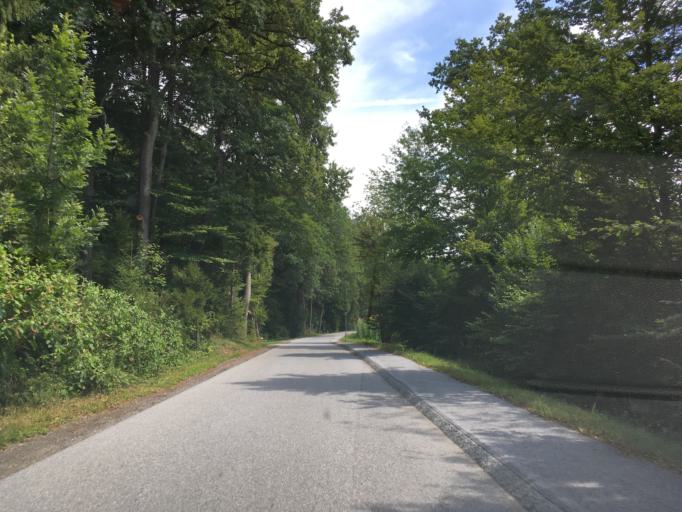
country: AT
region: Styria
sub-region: Politischer Bezirk Leibnitz
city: Pistorf
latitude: 46.7911
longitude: 15.3840
